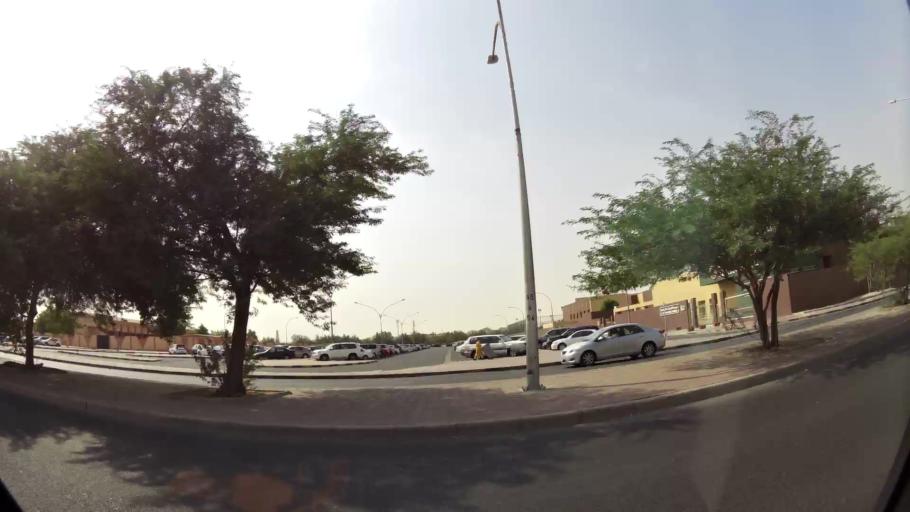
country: KW
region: Al Farwaniyah
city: Al Farwaniyah
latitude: 29.2506
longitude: 47.9293
